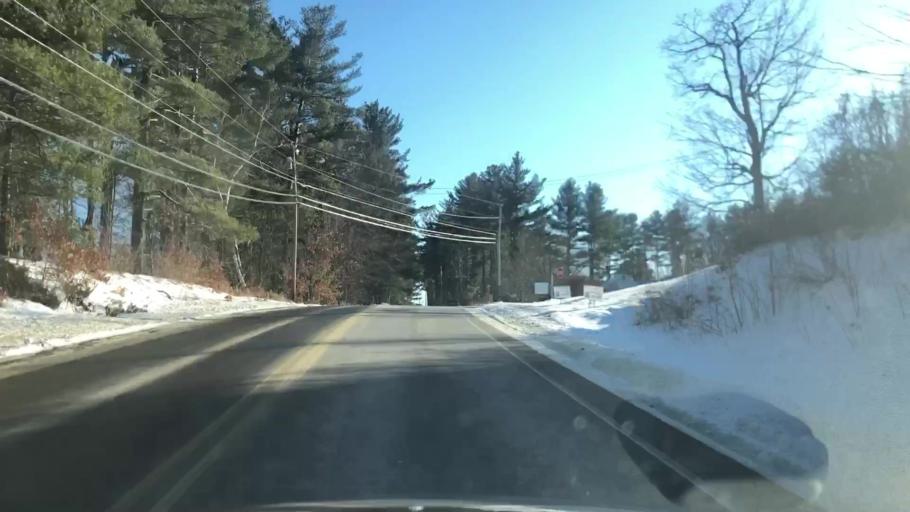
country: US
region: New Hampshire
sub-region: Hillsborough County
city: Wilton
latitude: 42.8363
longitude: -71.7055
